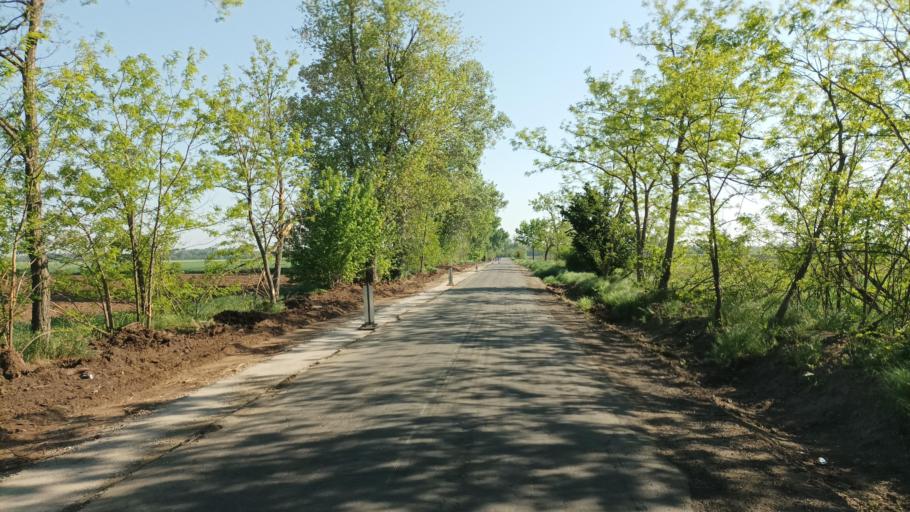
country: HU
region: Pest
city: Nyaregyhaza
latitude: 47.2857
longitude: 19.4904
